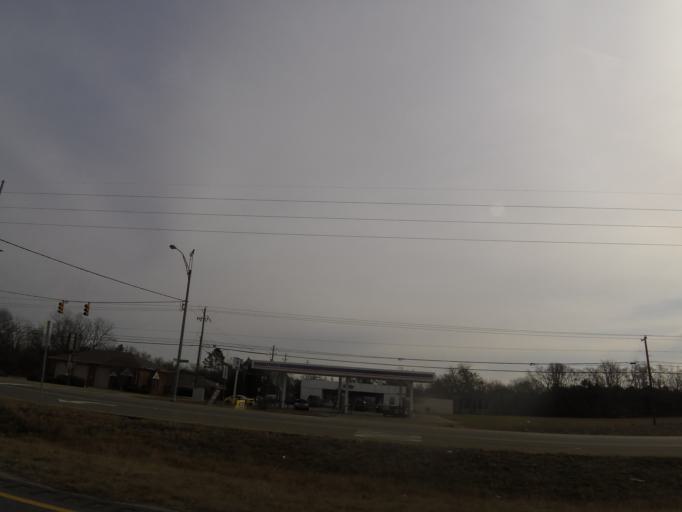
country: US
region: Alabama
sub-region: Montgomery County
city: Montgomery
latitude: 32.3353
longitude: -86.2291
